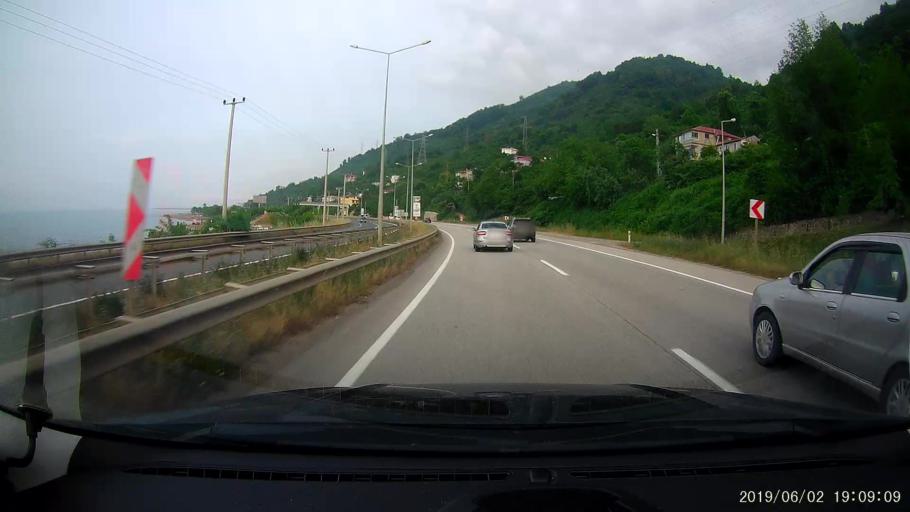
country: TR
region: Ordu
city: Gulyali
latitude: 40.9743
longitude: 38.0228
